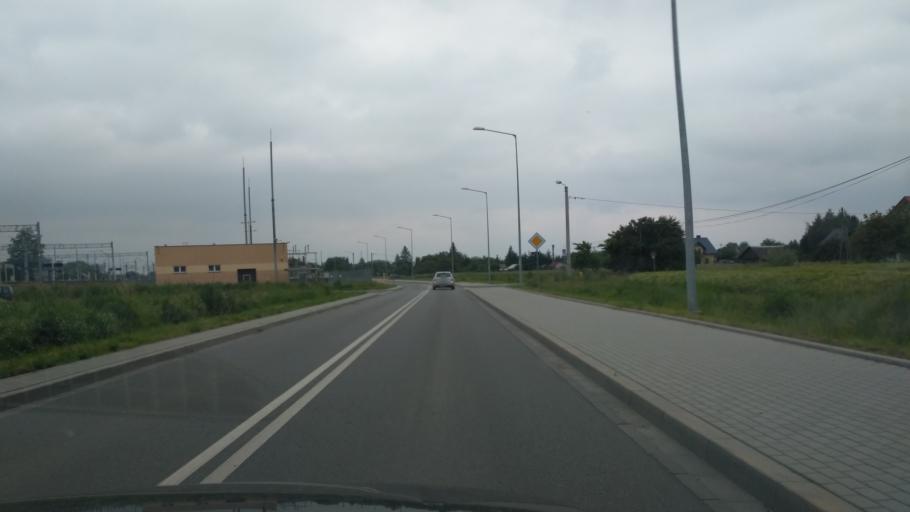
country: PL
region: Subcarpathian Voivodeship
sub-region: Powiat ropczycko-sedziszowski
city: Sedziszow Malopolski
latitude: 50.0760
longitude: 21.6912
